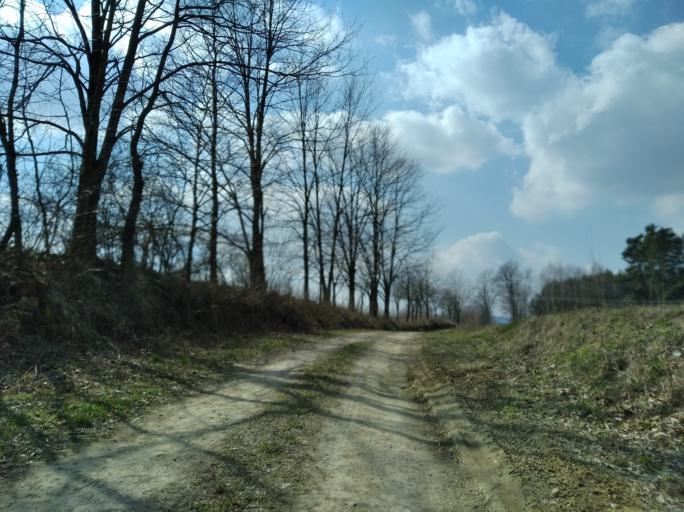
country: PL
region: Subcarpathian Voivodeship
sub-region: Powiat strzyzowski
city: Jawornik
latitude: 49.8235
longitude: 21.8568
